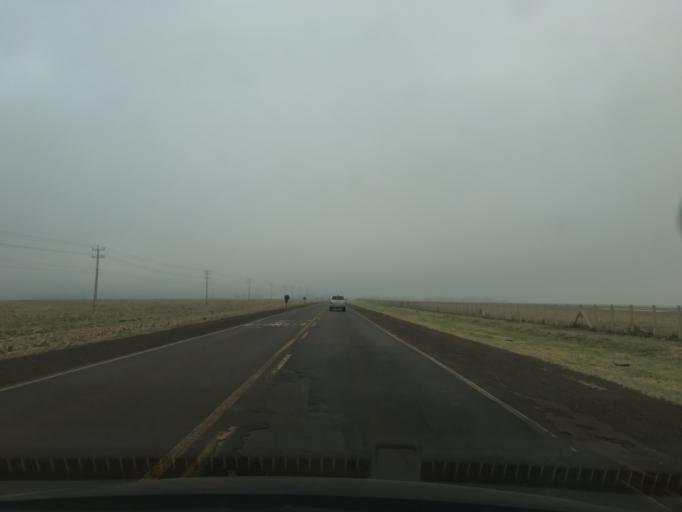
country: BR
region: Parana
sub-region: Toledo
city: Toledo
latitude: -24.6882
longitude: -53.6960
